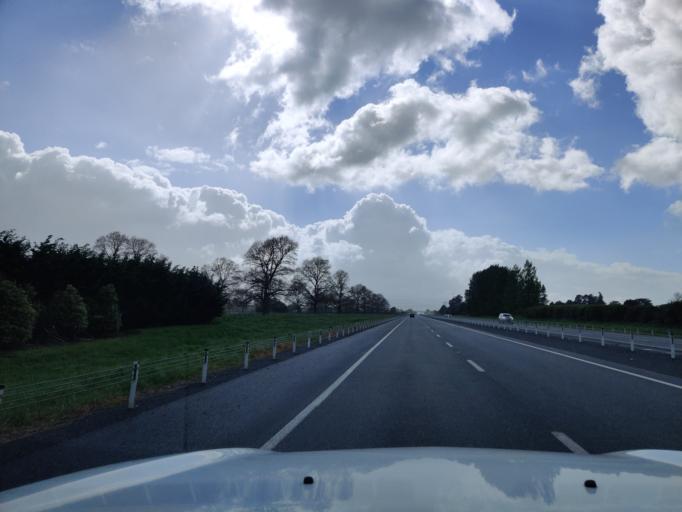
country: NZ
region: Waikato
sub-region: Waipa District
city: Cambridge
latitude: -37.8685
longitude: 175.4133
